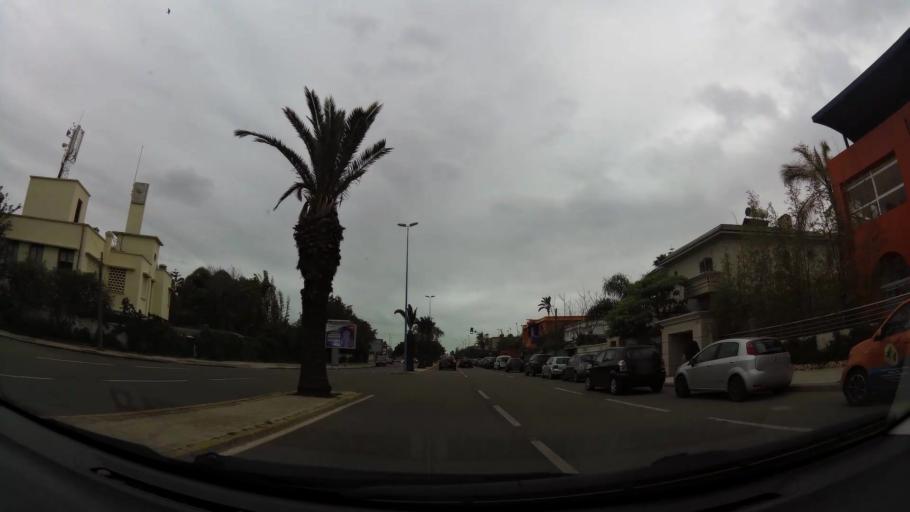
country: MA
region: Grand Casablanca
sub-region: Casablanca
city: Casablanca
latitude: 33.5946
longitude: -7.6546
